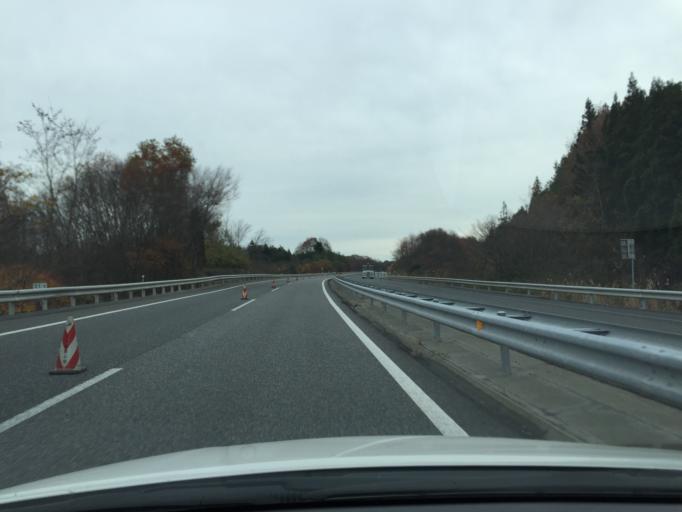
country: JP
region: Fukushima
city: Funehikimachi-funehiki
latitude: 37.2681
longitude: 140.6387
